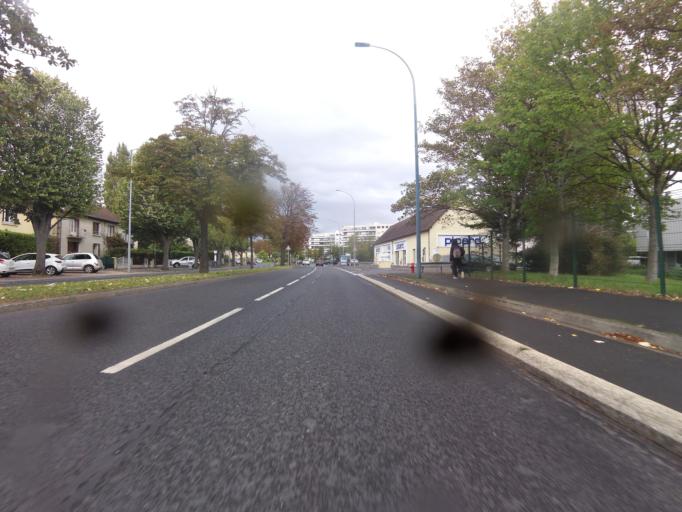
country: FR
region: Lower Normandy
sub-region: Departement du Calvados
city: Caen
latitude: 49.1874
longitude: -0.3795
